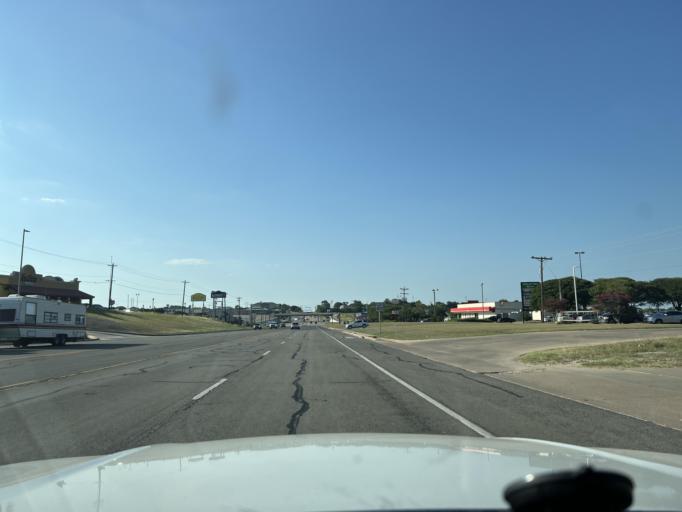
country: US
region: Texas
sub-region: Washington County
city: Brenham
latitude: 30.1381
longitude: -96.3956
